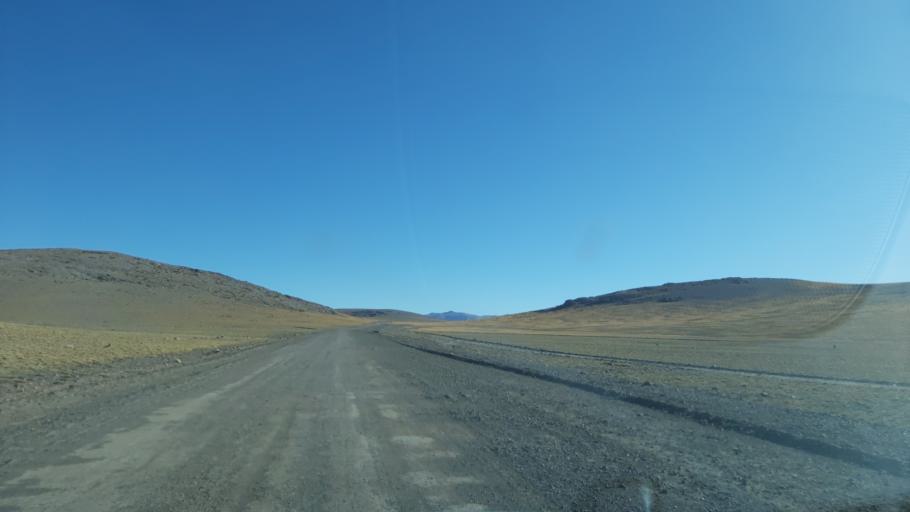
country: CL
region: Atacama
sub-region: Provincia de Chanaral
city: Diego de Almagro
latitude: -26.4595
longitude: -69.2918
